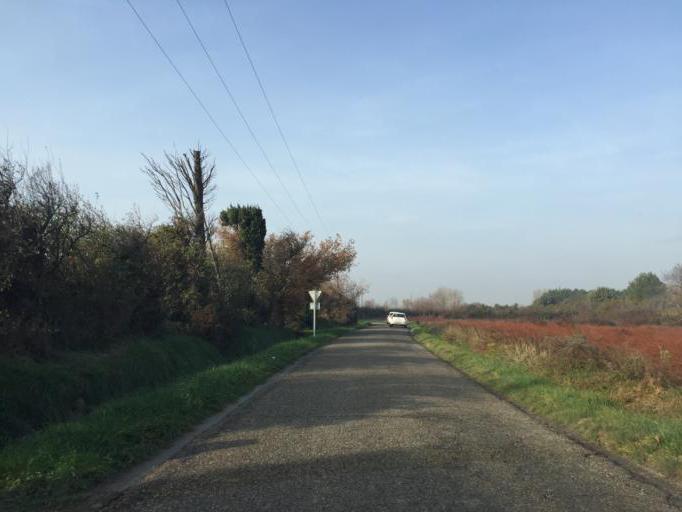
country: FR
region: Provence-Alpes-Cote d'Azur
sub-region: Departement du Vaucluse
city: Jonquieres
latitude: 44.1262
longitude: 4.8957
